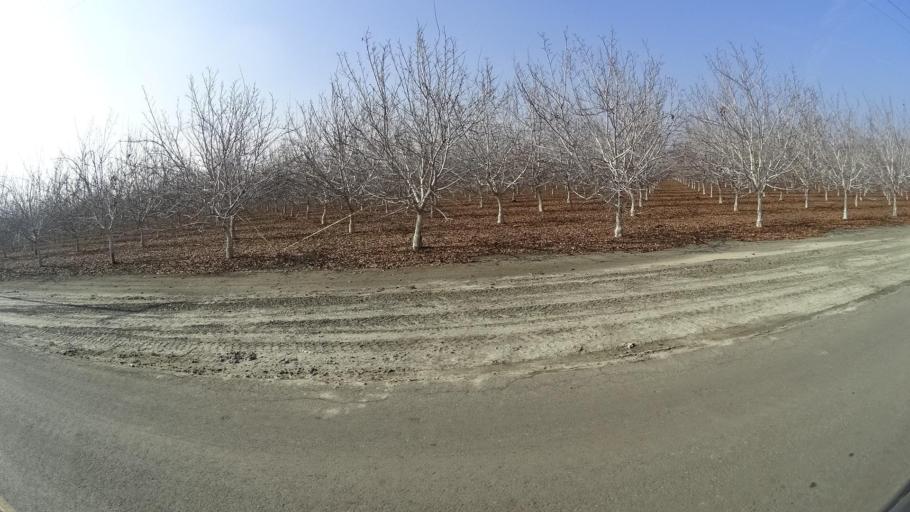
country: US
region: California
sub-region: Kern County
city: Buttonwillow
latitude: 35.3649
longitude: -119.4123
